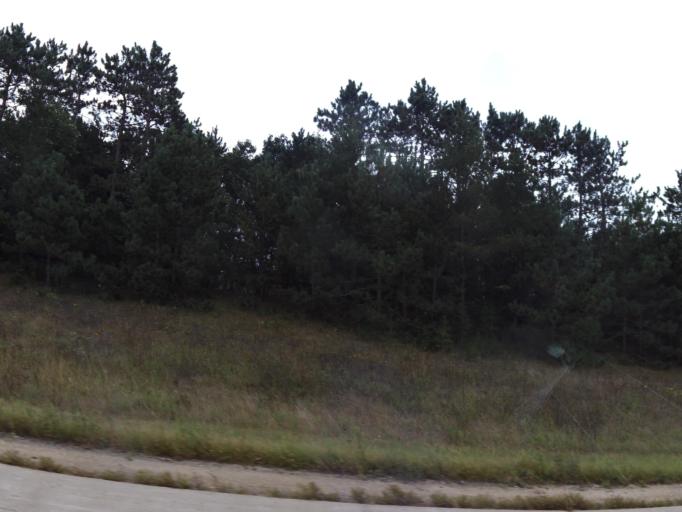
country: US
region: Wisconsin
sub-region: Monroe County
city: Sparta
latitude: 43.9260
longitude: -90.7967
